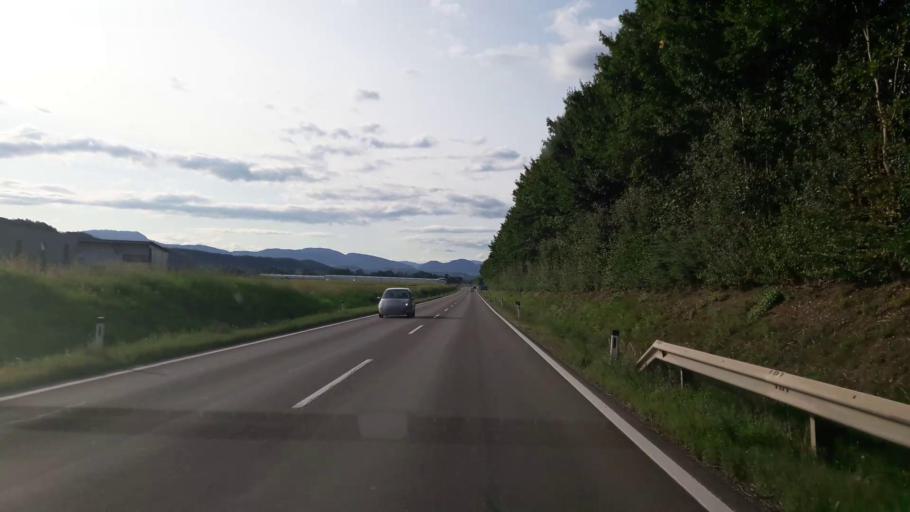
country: AT
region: Styria
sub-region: Politischer Bezirk Weiz
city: Gleisdorf
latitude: 47.1238
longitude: 15.6947
